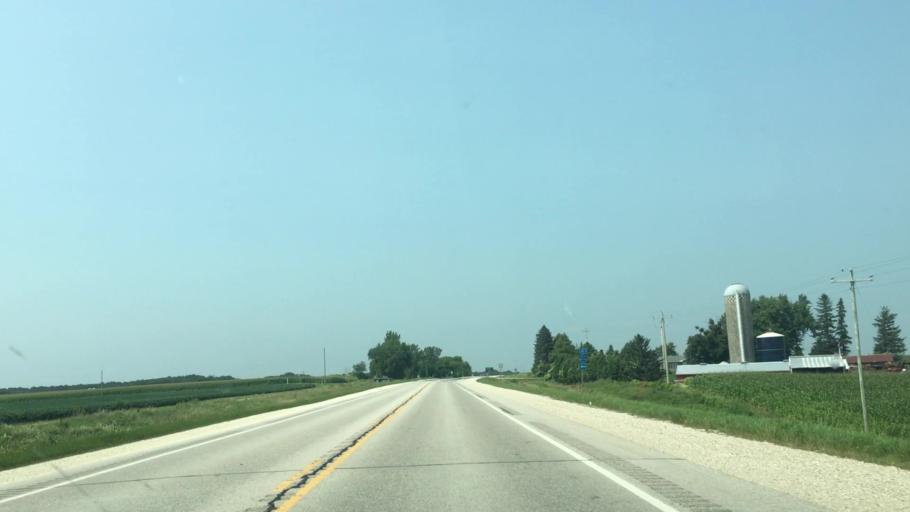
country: US
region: Iowa
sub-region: Winneshiek County
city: Decorah
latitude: 43.2014
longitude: -91.8764
